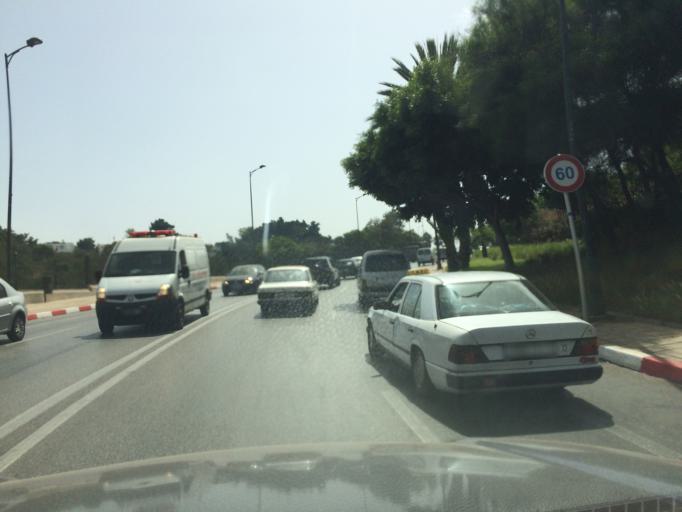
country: MA
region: Rabat-Sale-Zemmour-Zaer
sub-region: Rabat
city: Rabat
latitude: 34.0180
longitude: -6.8204
